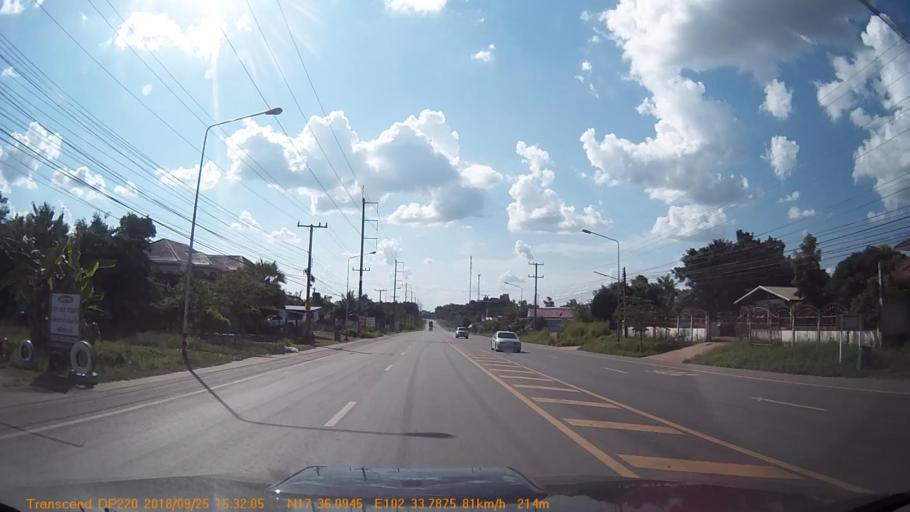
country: TH
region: Changwat Udon Thani
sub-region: Amphoe Ban Phue
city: Ban Phue
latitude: 17.6018
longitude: 102.5625
